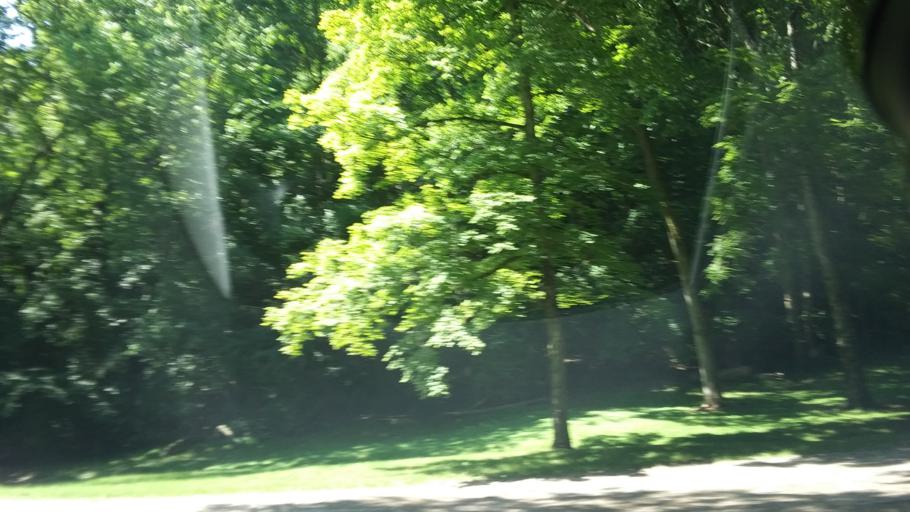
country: US
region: Tennessee
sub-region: Davidson County
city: Forest Hills
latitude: 36.0638
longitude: -86.8840
